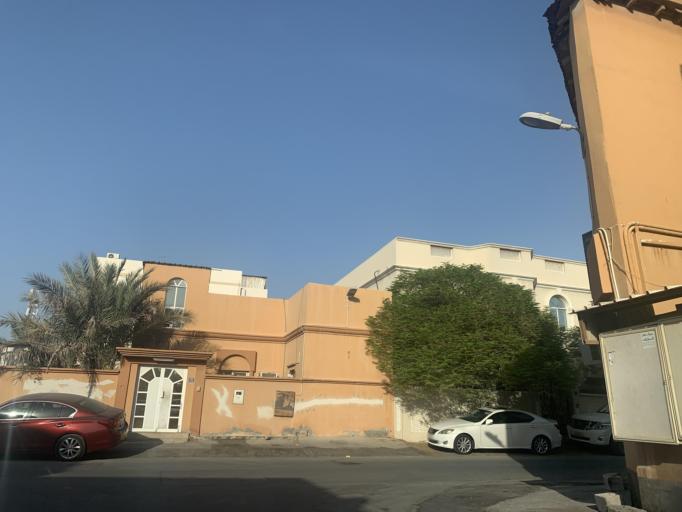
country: BH
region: Northern
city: Madinat `Isa
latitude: 26.1945
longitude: 50.4825
